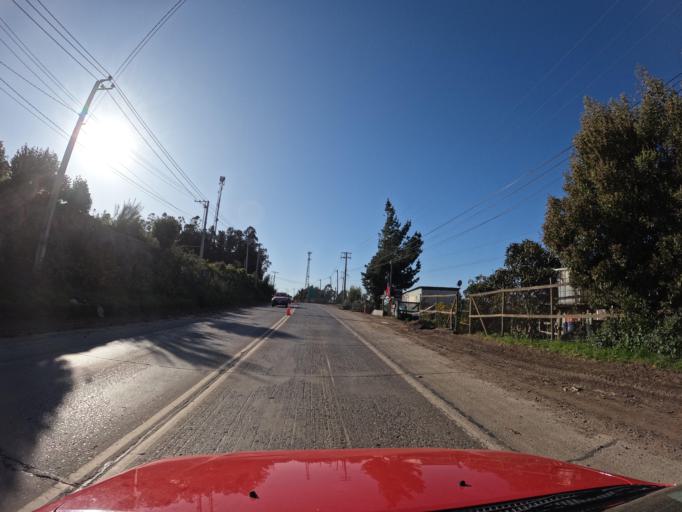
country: CL
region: Maule
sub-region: Provincia de Talca
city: Constitucion
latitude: -35.3702
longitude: -72.3976
